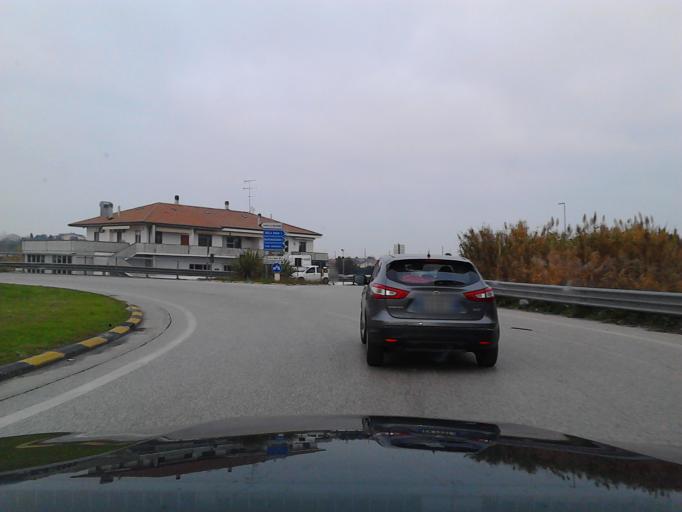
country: IT
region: Abruzzo
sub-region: Provincia di Teramo
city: Alba Adriatica
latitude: 42.8357
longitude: 13.9148
